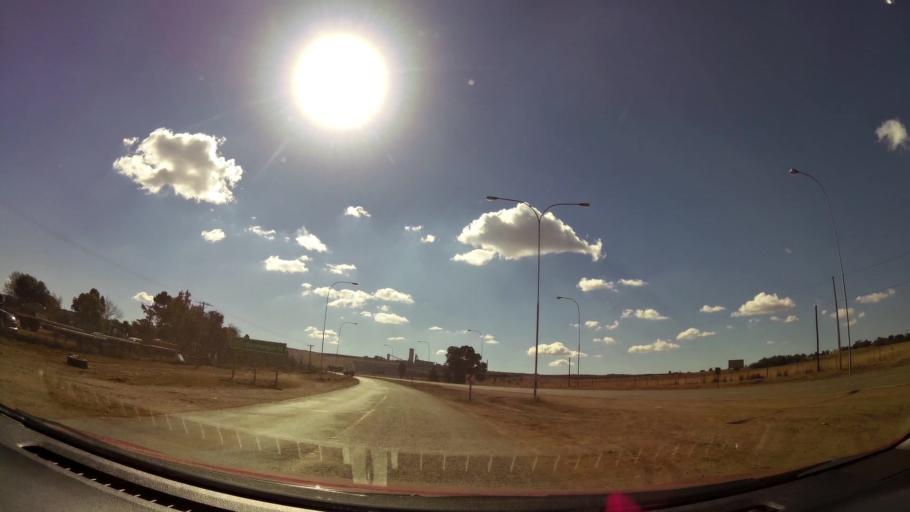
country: ZA
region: North-West
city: Fochville
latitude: -26.4405
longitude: 27.4835
